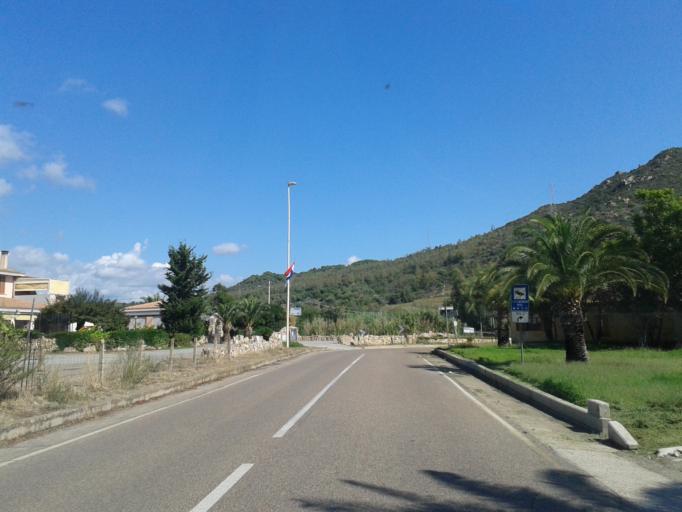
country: IT
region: Sardinia
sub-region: Provincia di Cagliari
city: Castiadas
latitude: 39.2089
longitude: 9.5414
